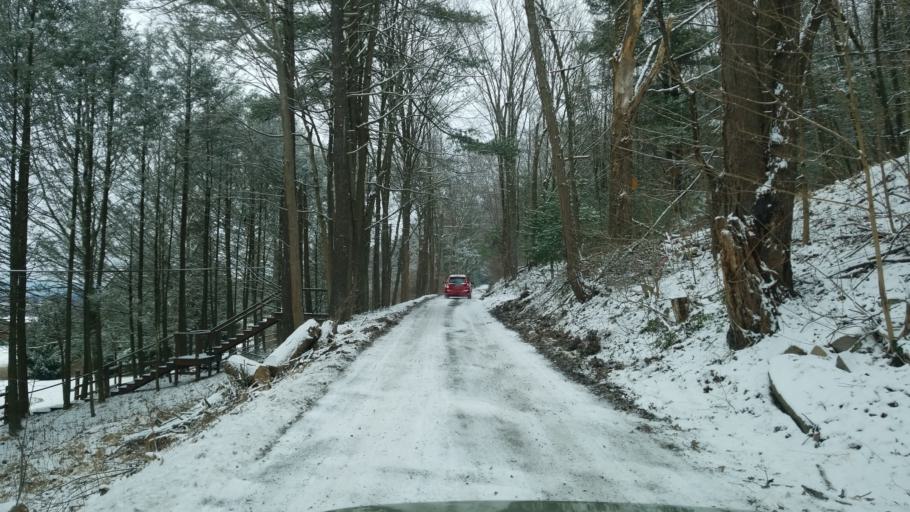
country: US
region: Pennsylvania
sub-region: Centre County
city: Centre Hall
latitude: 40.7719
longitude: -77.6728
